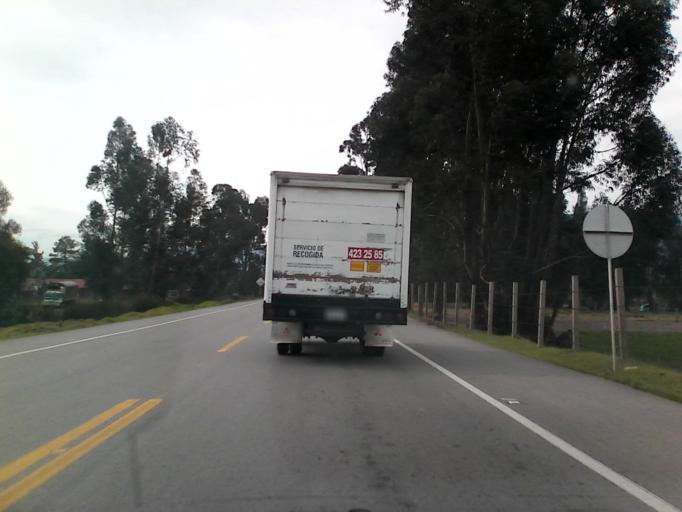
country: CO
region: Boyaca
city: Tibasosa
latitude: 5.7854
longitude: -72.9968
